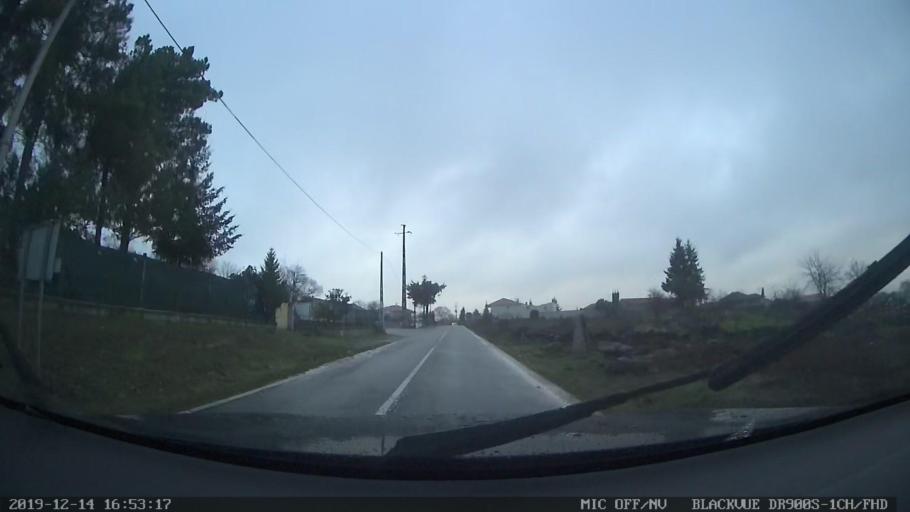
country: PT
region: Vila Real
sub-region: Murca
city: Murca
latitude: 41.4295
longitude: -7.5165
